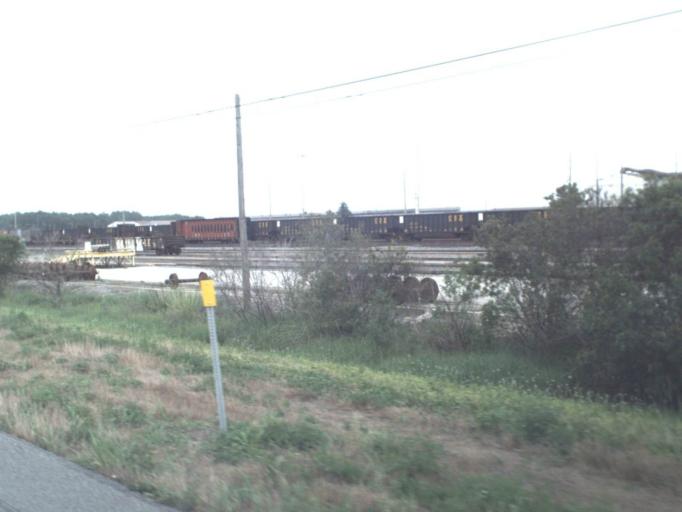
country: US
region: Florida
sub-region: Duval County
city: Baldwin
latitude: 30.2805
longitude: -81.9840
